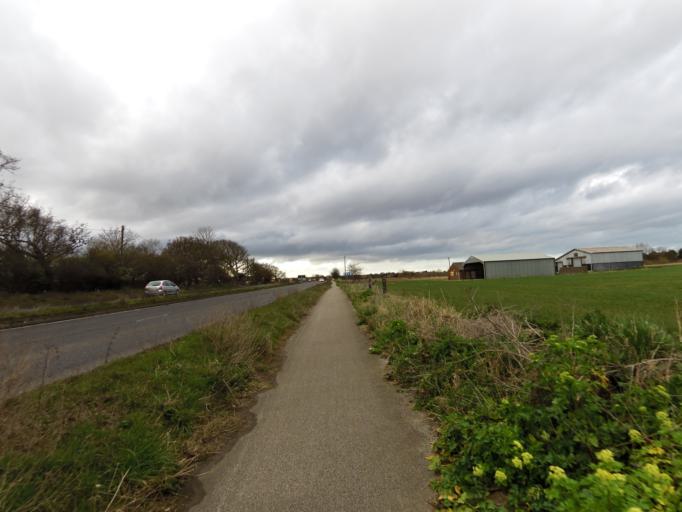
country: GB
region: England
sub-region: Norfolk
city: Hopton on Sea
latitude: 52.5516
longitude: 1.7183
